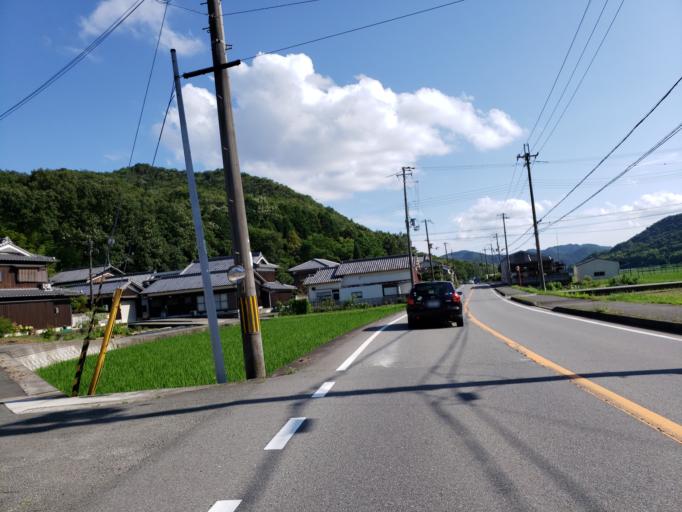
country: JP
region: Hyogo
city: Kakogawacho-honmachi
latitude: 34.8750
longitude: 134.7975
